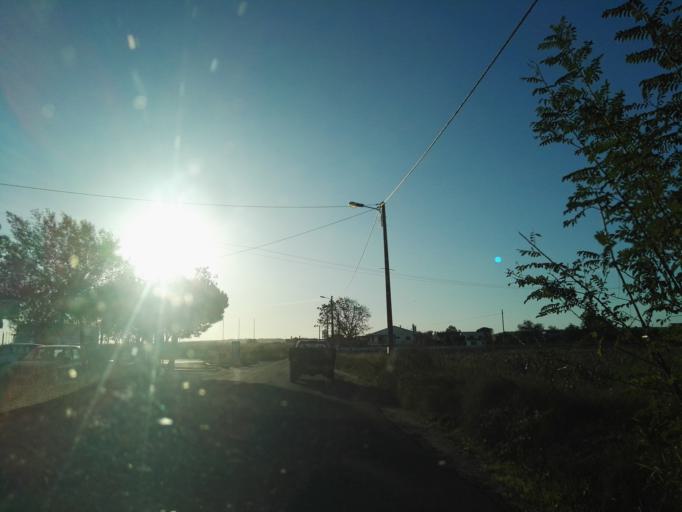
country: PT
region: Santarem
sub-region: Golega
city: Golega
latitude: 39.3432
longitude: -8.5449
